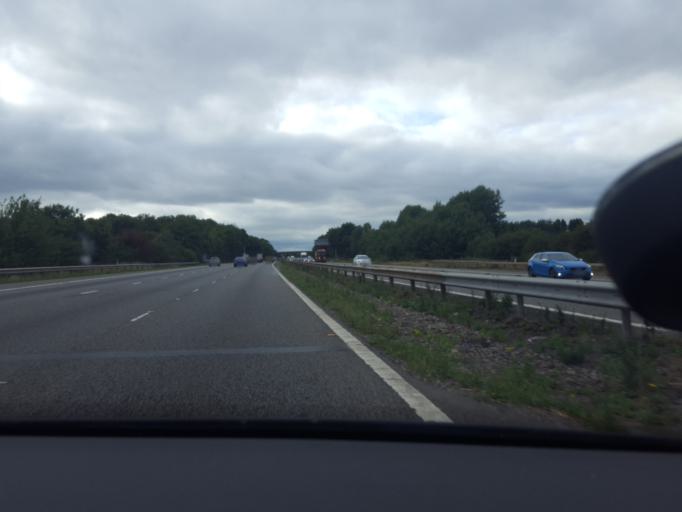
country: GB
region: England
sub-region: Leicestershire
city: Markfield
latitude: 52.6625
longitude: -1.2655
